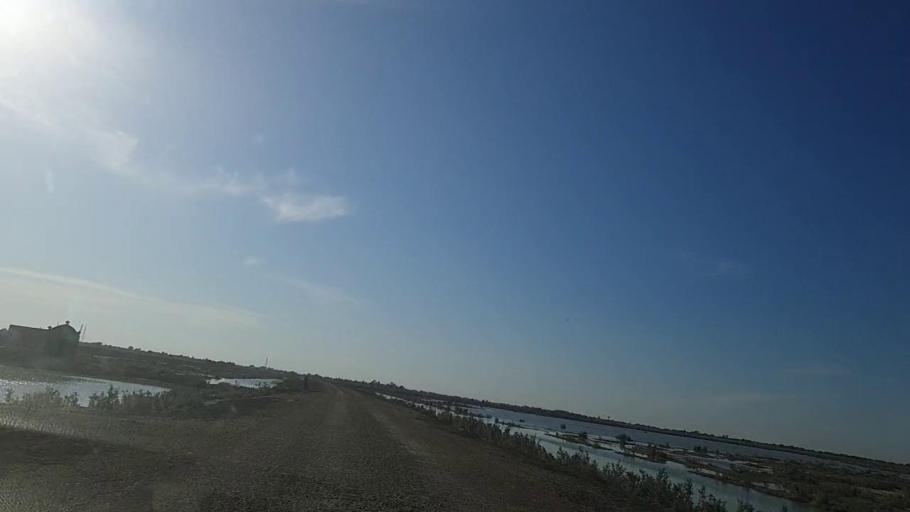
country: PK
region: Sindh
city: Pithoro
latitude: 25.5108
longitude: 69.4075
